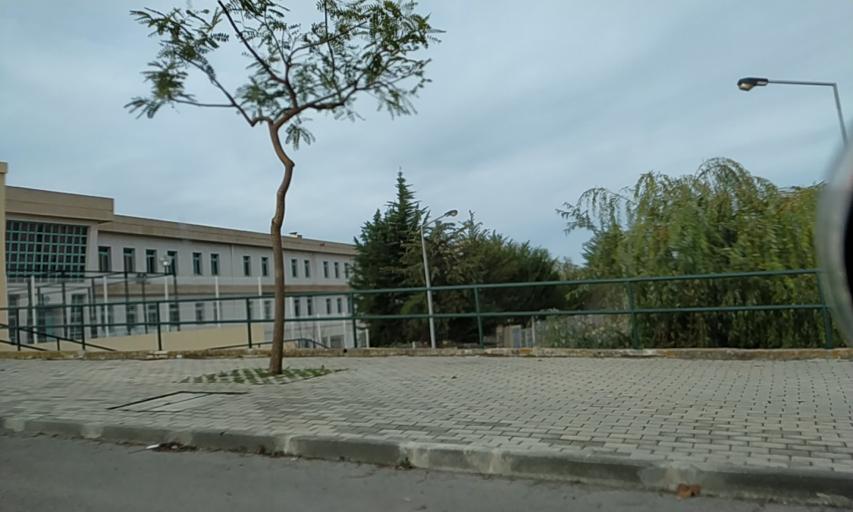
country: PT
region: Setubal
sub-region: Setubal
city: Setubal
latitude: 38.5197
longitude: -8.8697
